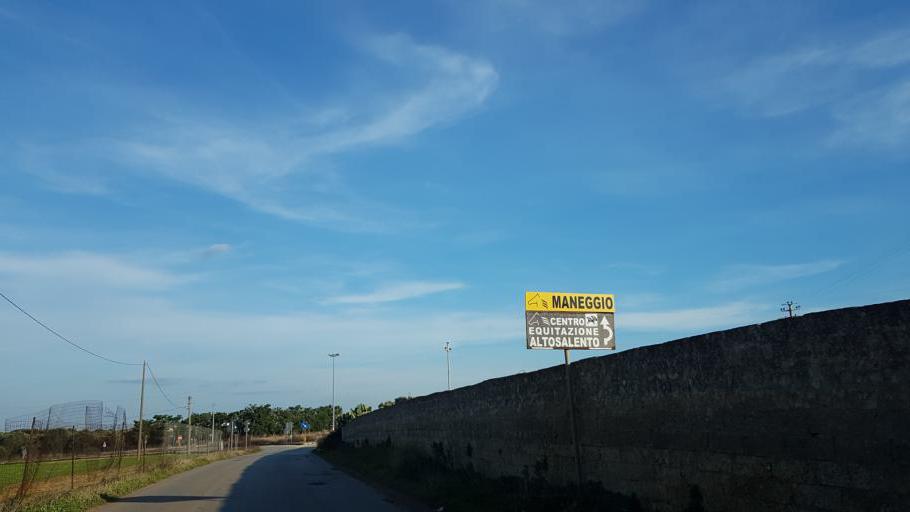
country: IT
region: Apulia
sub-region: Provincia di Brindisi
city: San Vito dei Normanni
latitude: 40.7040
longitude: 17.7216
